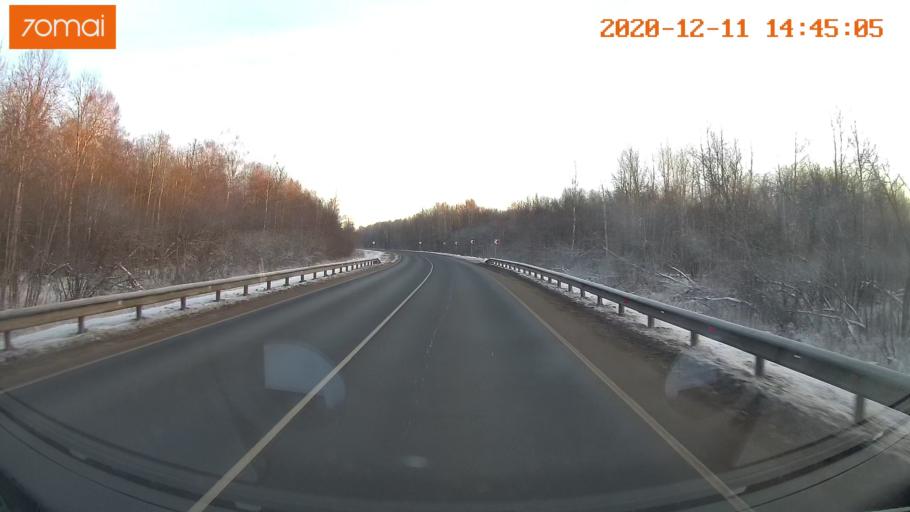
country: RU
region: Kostroma
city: Volgorechensk
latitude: 57.4574
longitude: 41.1102
